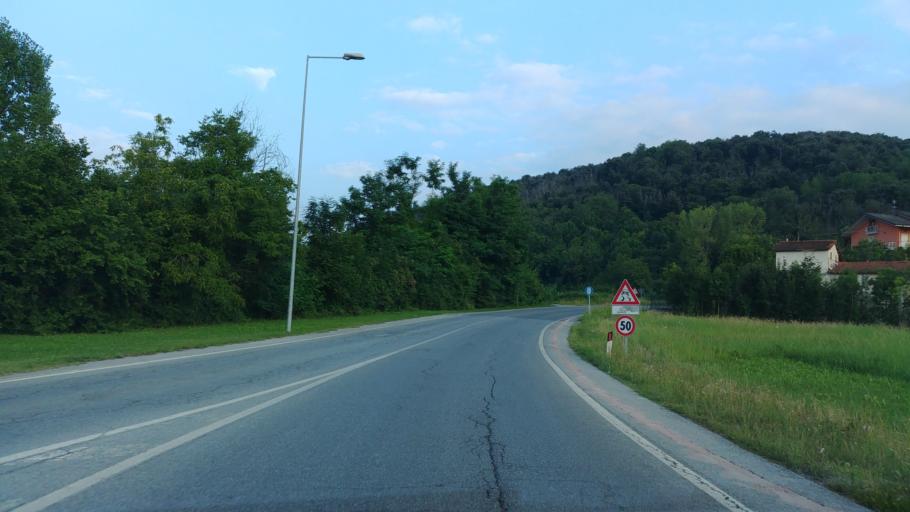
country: IT
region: Piedmont
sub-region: Provincia di Cuneo
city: Peveragno
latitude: 44.3350
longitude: 7.6060
